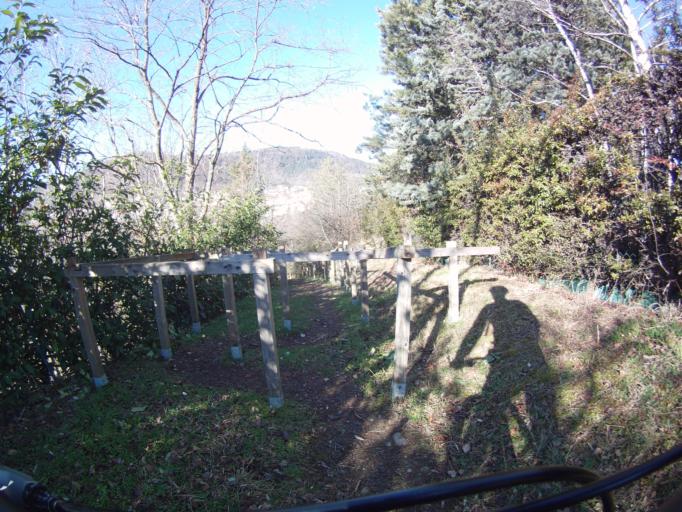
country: FR
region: Auvergne
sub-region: Departement du Puy-de-Dome
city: Ceyrat
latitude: 45.7296
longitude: 3.0714
